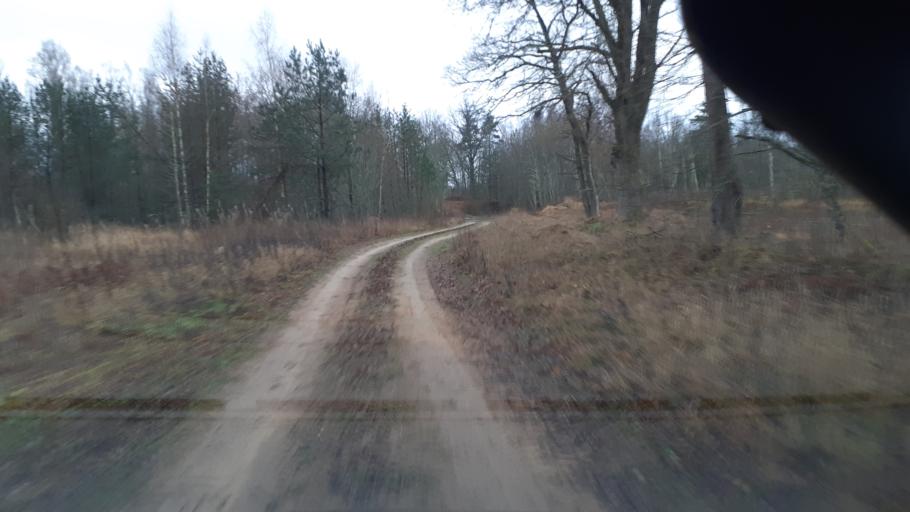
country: LV
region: Kuldigas Rajons
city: Kuldiga
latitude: 56.8801
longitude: 21.7705
